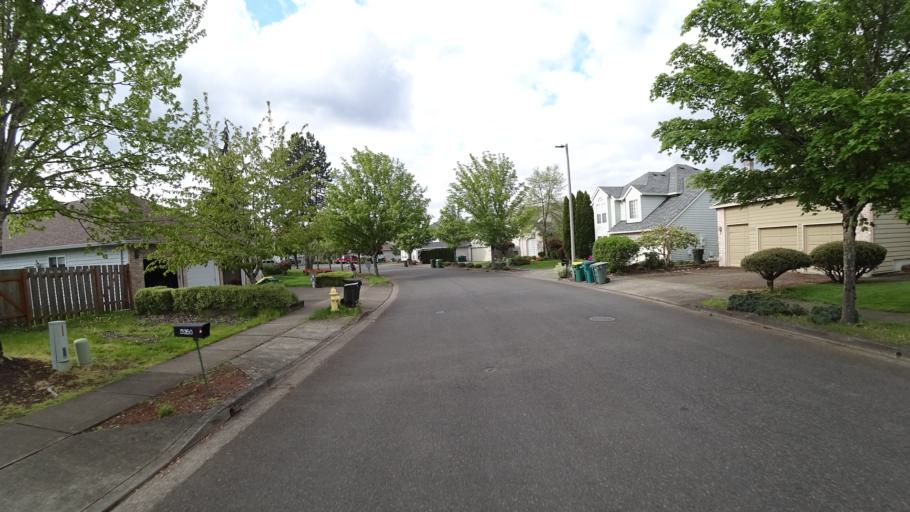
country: US
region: Oregon
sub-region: Washington County
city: Beaverton
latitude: 45.4558
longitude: -122.8341
